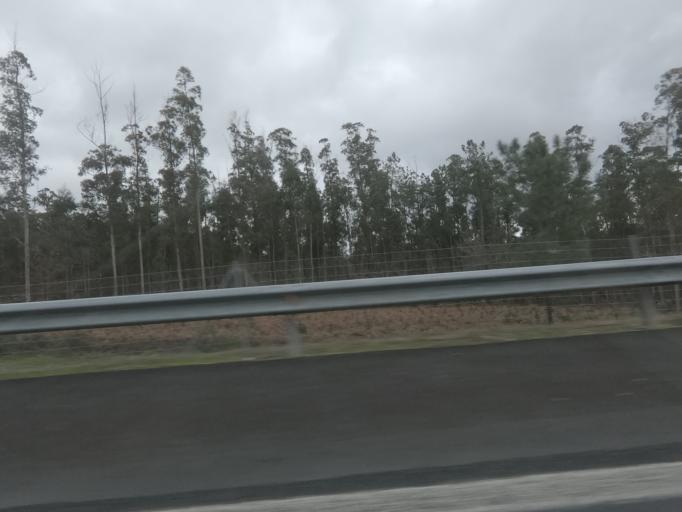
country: ES
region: Galicia
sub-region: Provincia da Coruna
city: Vedra
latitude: 42.8202
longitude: -8.4919
